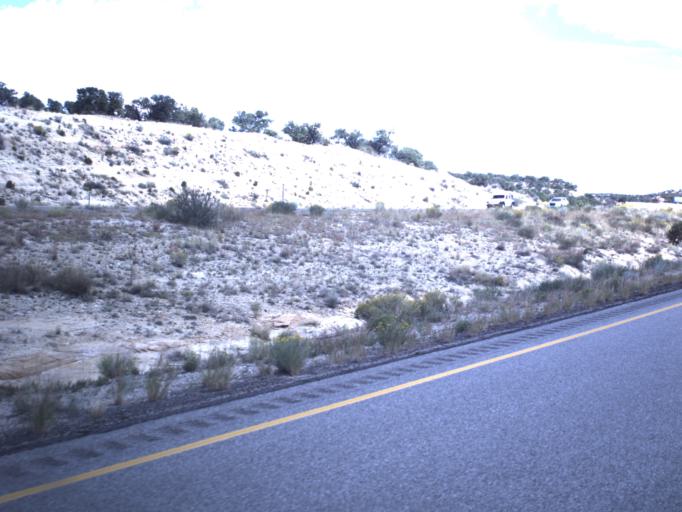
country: US
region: Utah
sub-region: Emery County
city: Ferron
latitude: 38.8594
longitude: -110.8388
